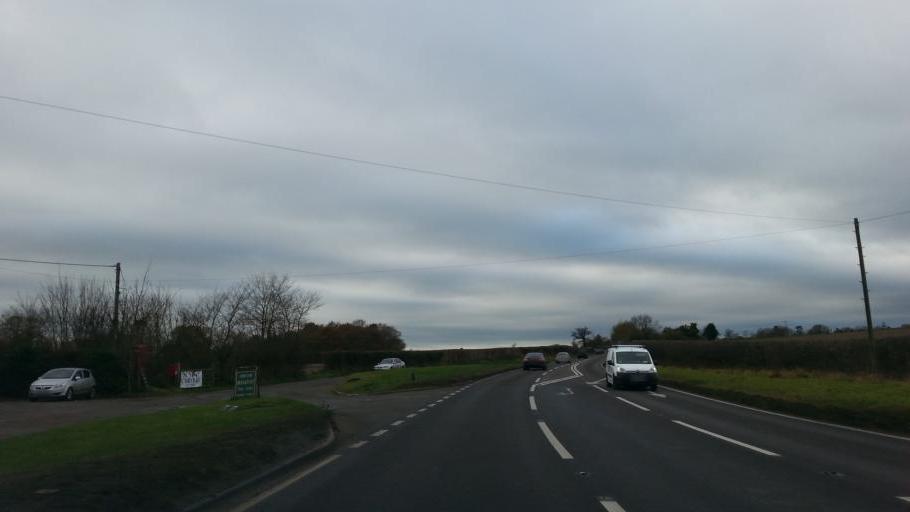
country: GB
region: England
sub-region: Norfolk
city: Diss
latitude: 52.3631
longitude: 1.1800
